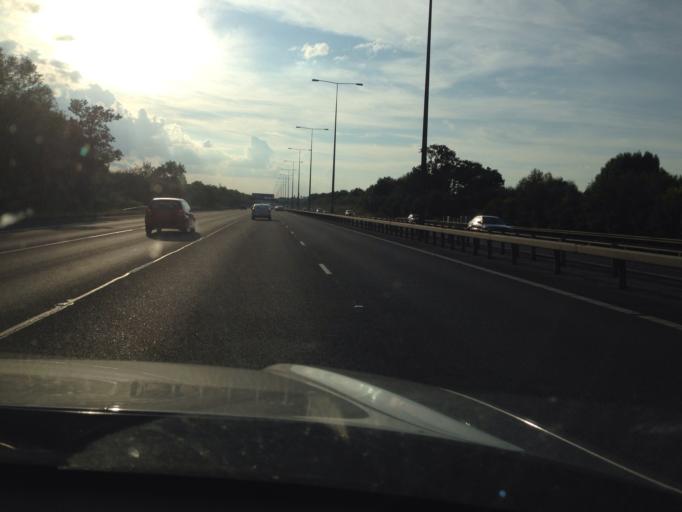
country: GB
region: England
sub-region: Buckinghamshire
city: Seer Green
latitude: 51.5861
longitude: -0.6003
